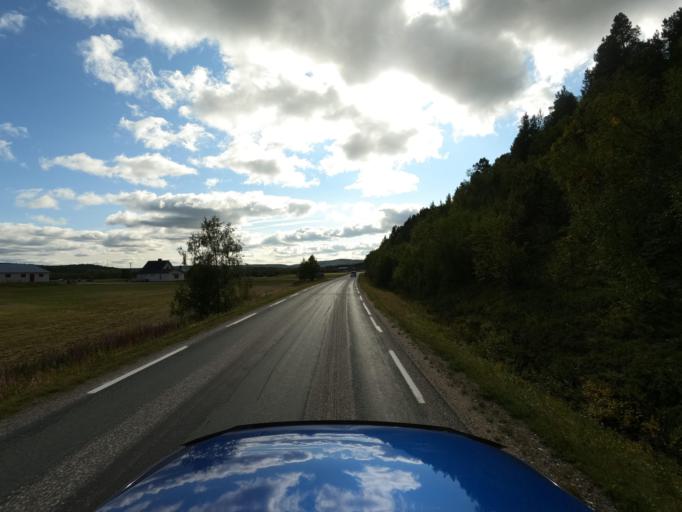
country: NO
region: Finnmark Fylke
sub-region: Karasjok
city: Karasjohka
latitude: 69.4115
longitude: 25.8047
